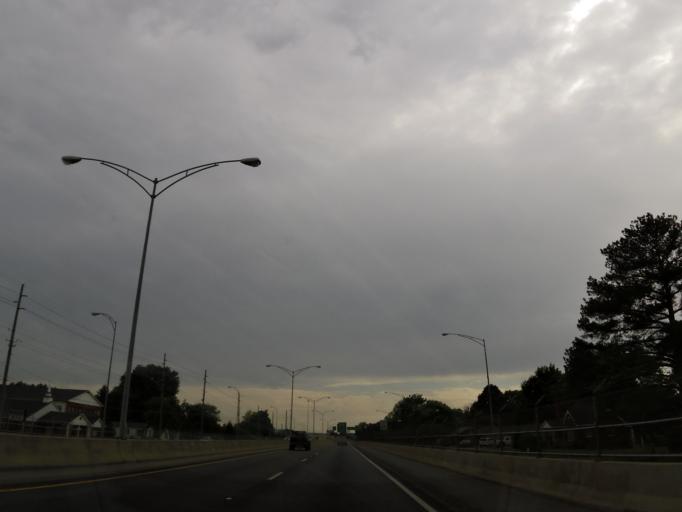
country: US
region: Alabama
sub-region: Madison County
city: Huntsville
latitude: 34.7535
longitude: -86.5719
